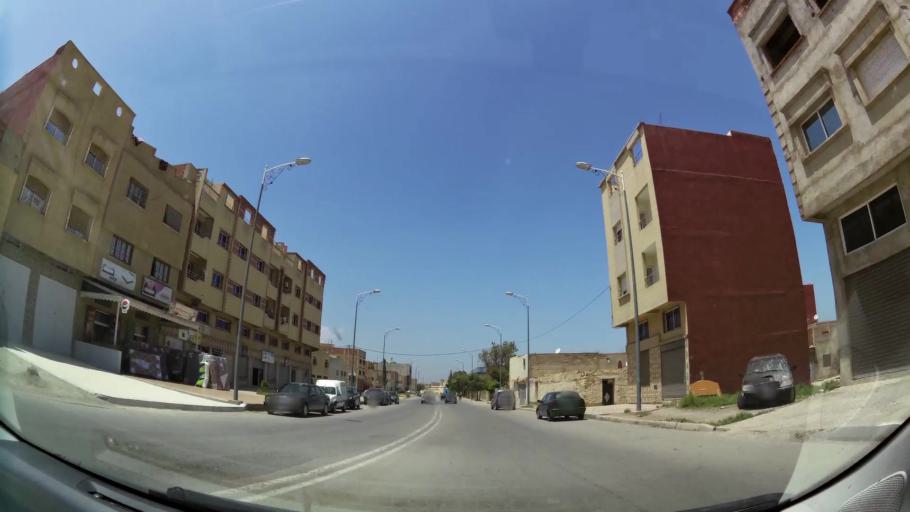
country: MA
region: Oriental
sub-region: Oujda-Angad
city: Oujda
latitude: 34.6998
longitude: -1.8928
